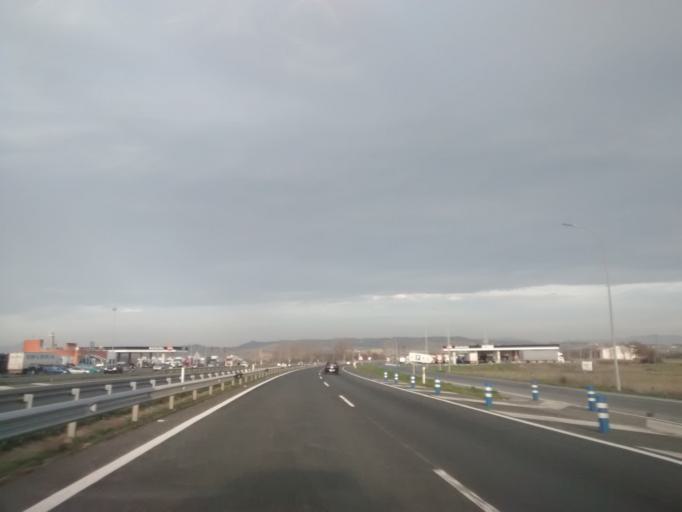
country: ES
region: Basque Country
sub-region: Provincia de Alava
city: Gasteiz / Vitoria
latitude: 42.8760
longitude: -2.7156
